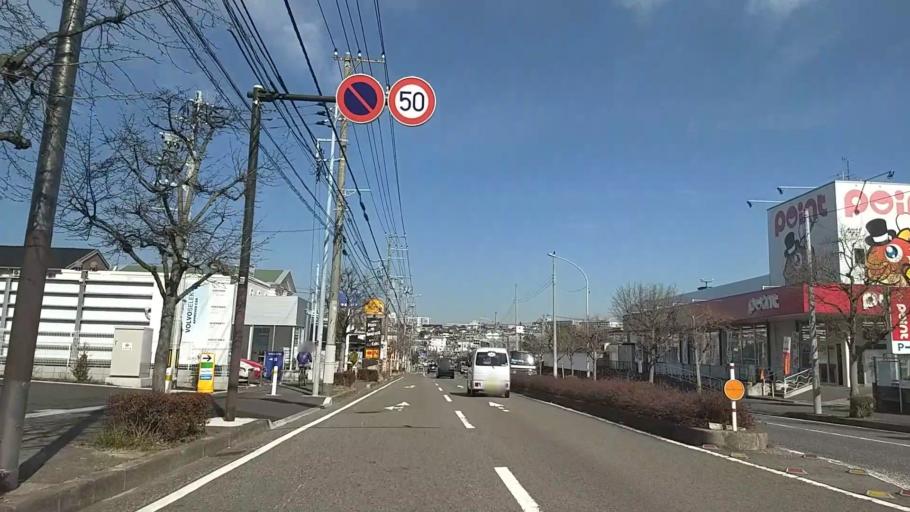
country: JP
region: Kanagawa
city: Kamakura
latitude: 35.3786
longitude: 139.5798
